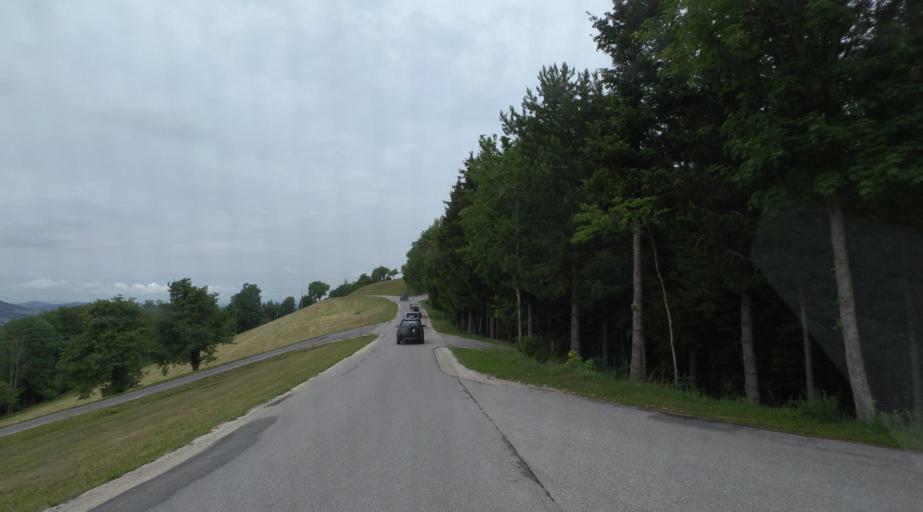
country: AT
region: Upper Austria
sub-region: Politischer Bezirk Kirchdorf an der Krems
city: Micheldorf in Oberoesterreich
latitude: 47.9356
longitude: 14.1687
